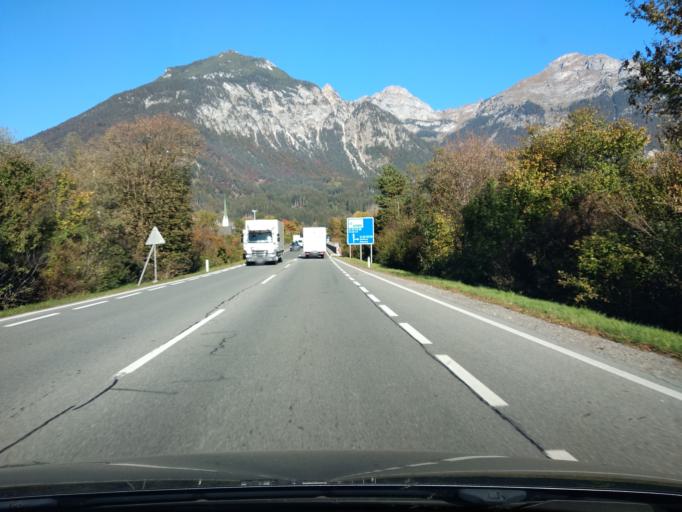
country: AT
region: Tyrol
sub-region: Politischer Bezirk Schwaz
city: Wiesing
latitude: 47.3994
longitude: 11.8054
